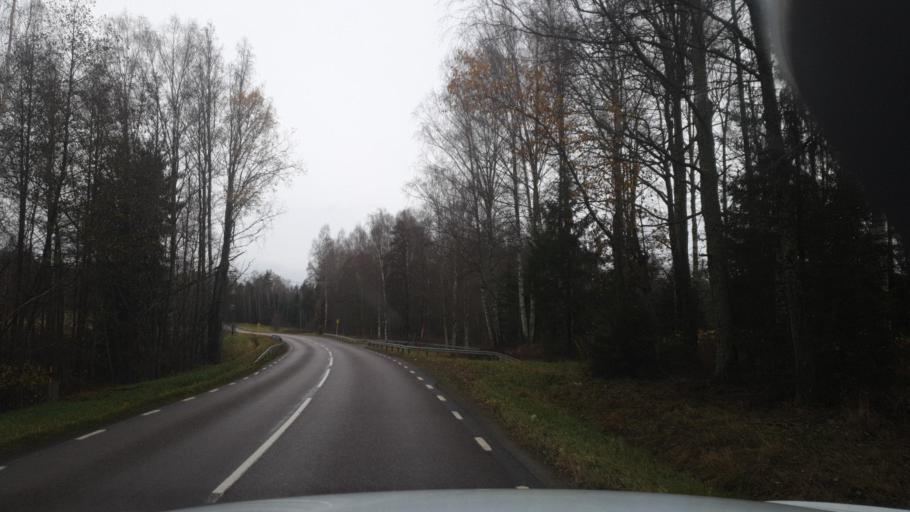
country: SE
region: Vaermland
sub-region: Arvika Kommun
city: Arvika
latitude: 59.5830
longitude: 12.5545
